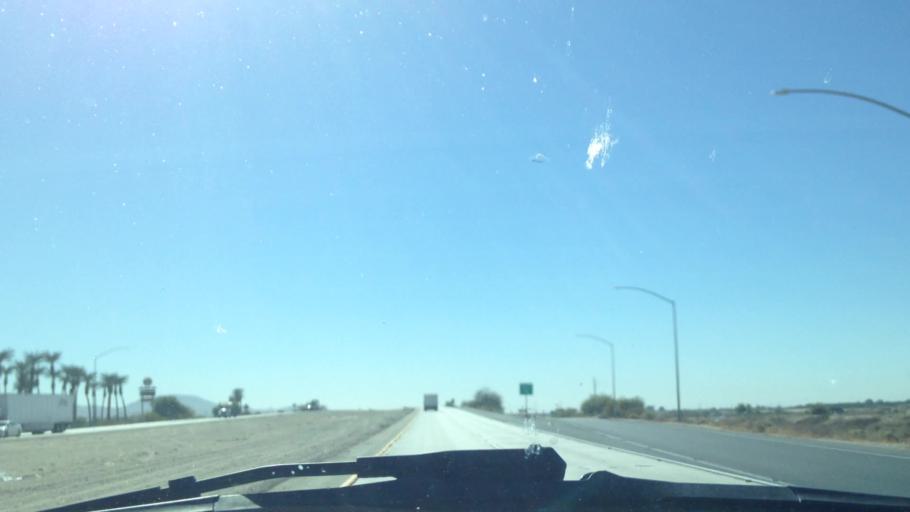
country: US
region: California
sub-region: Riverside County
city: Indio
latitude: 33.7112
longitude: -116.1855
